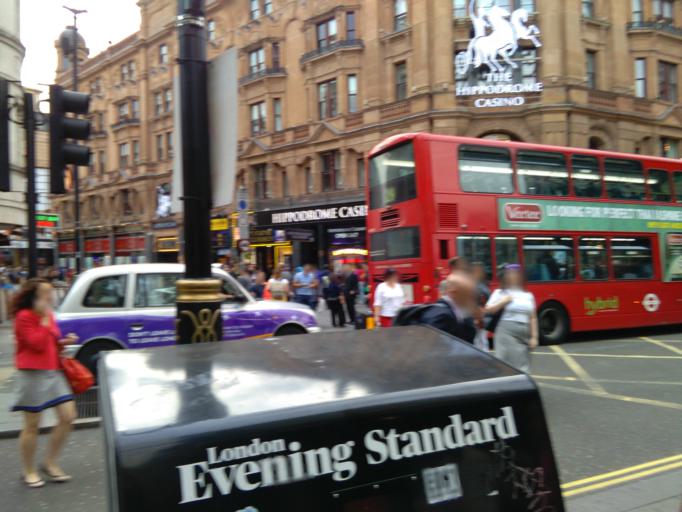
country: GB
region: England
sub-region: Greater London
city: London
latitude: 51.5114
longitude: -0.1283
